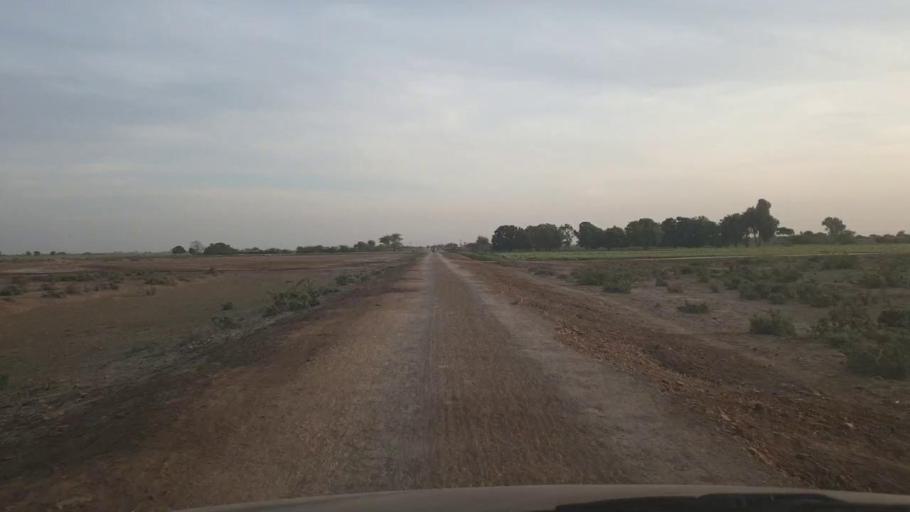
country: PK
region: Sindh
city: Kunri
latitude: 25.2159
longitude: 69.5740
